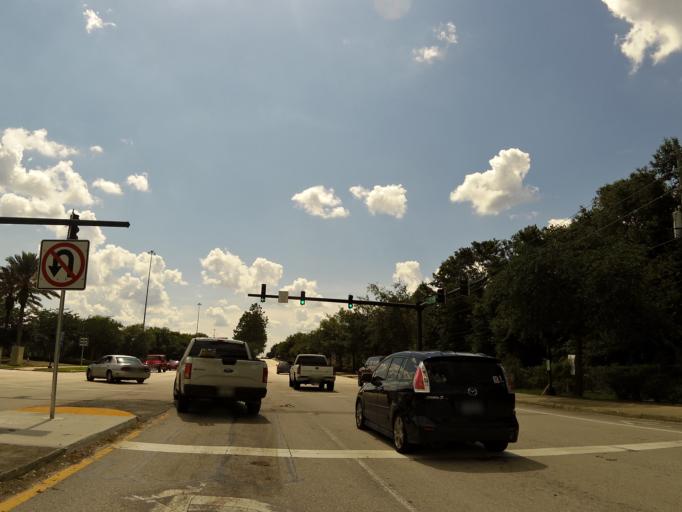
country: US
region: Florida
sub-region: Saint Johns County
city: Fruit Cove
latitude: 30.1412
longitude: -81.5365
